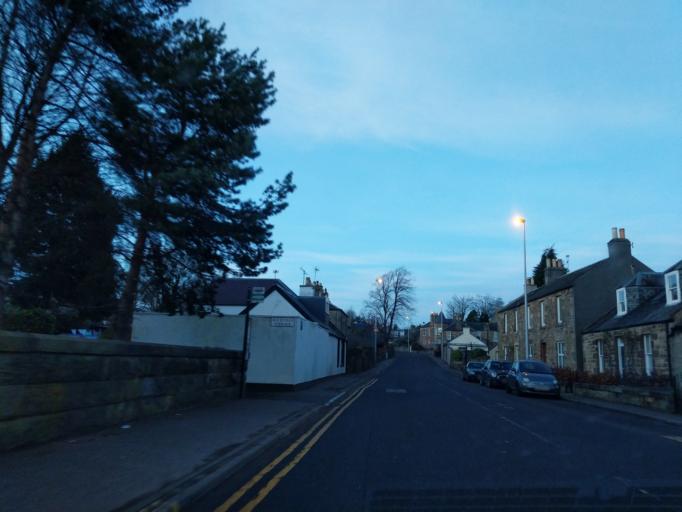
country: GB
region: Scotland
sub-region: Midlothian
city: Bonnyrigg
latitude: 55.8781
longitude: -3.1078
